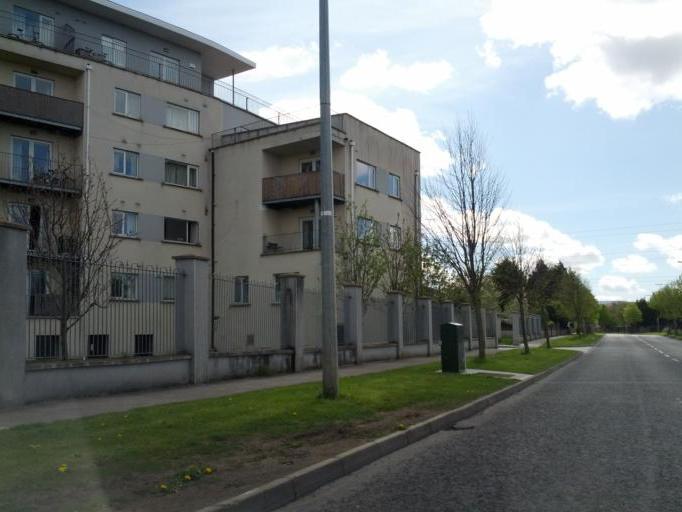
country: IE
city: Cherry Orchard
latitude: 53.3274
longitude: -6.3837
